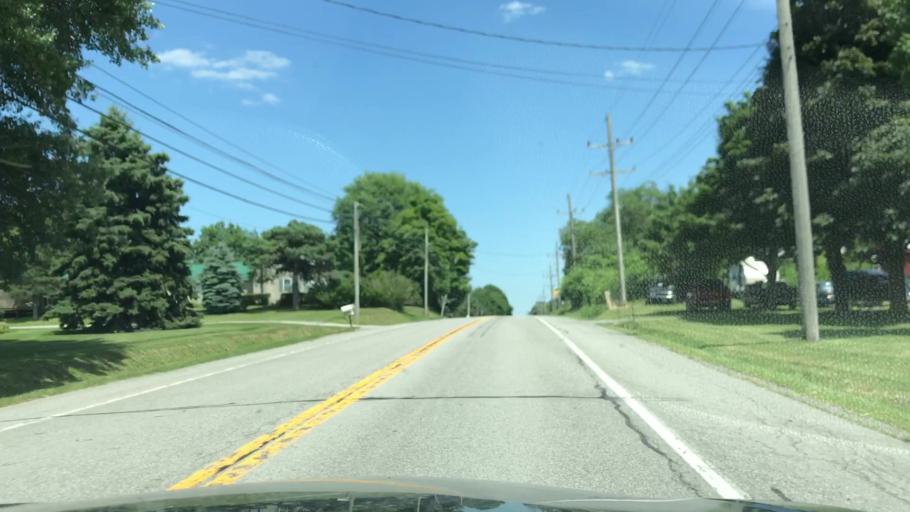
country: US
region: New York
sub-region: Wyoming County
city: Perry
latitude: 42.7481
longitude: -78.0144
